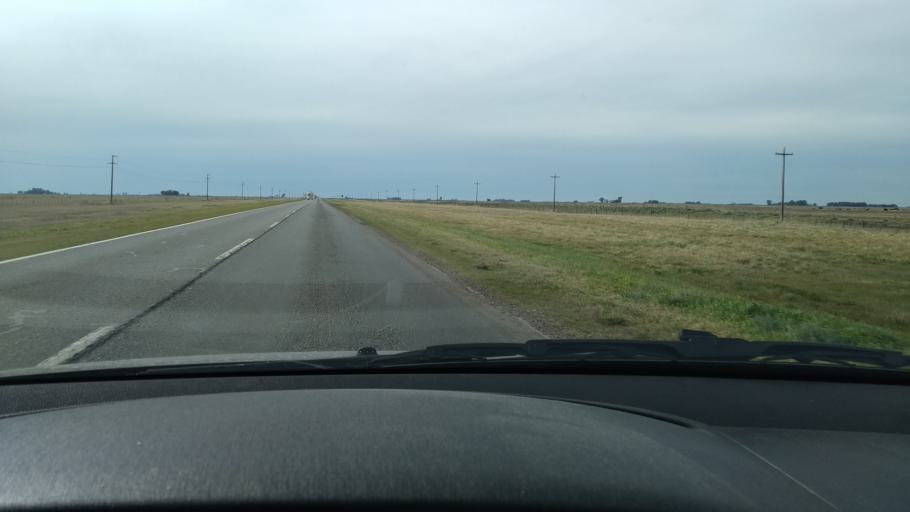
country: AR
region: Buenos Aires
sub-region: Partido de Azul
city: Azul
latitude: -36.6998
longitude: -59.7493
